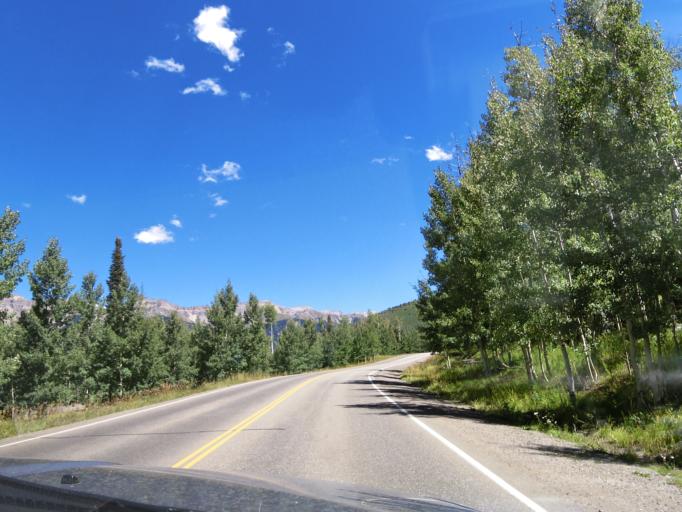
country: US
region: Colorado
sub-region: San Miguel County
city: Mountain Village
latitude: 37.9341
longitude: -107.8596
